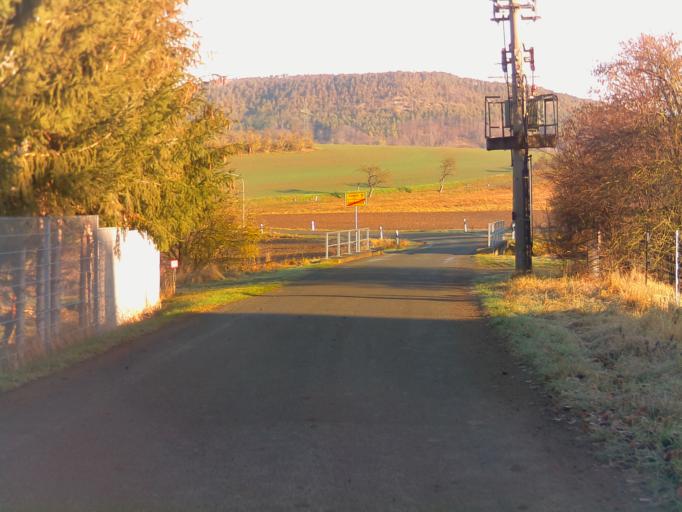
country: DE
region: Thuringia
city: Gumperda
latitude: 50.8082
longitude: 11.5053
